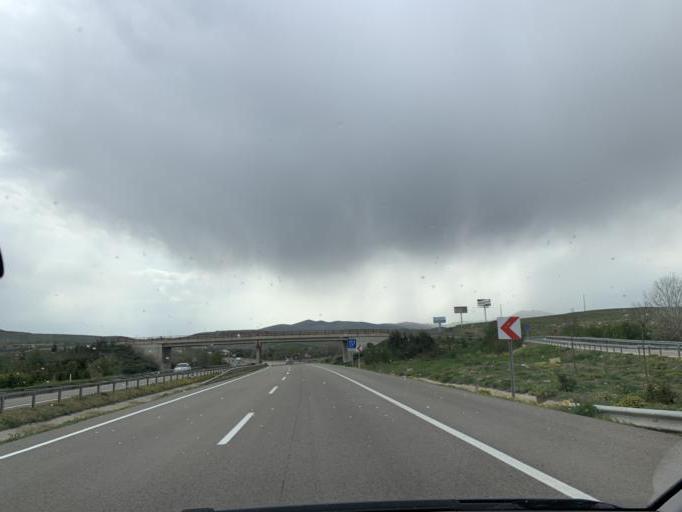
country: TR
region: Eskisehir
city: Sivrihisar
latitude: 39.5296
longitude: 31.6287
